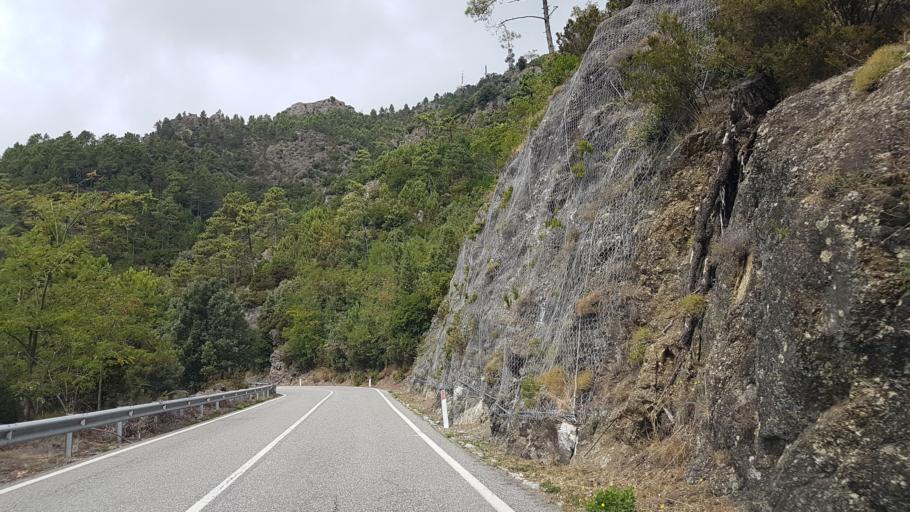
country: IT
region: Liguria
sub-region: Provincia di La Spezia
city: Framura
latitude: 44.2484
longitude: 9.5747
